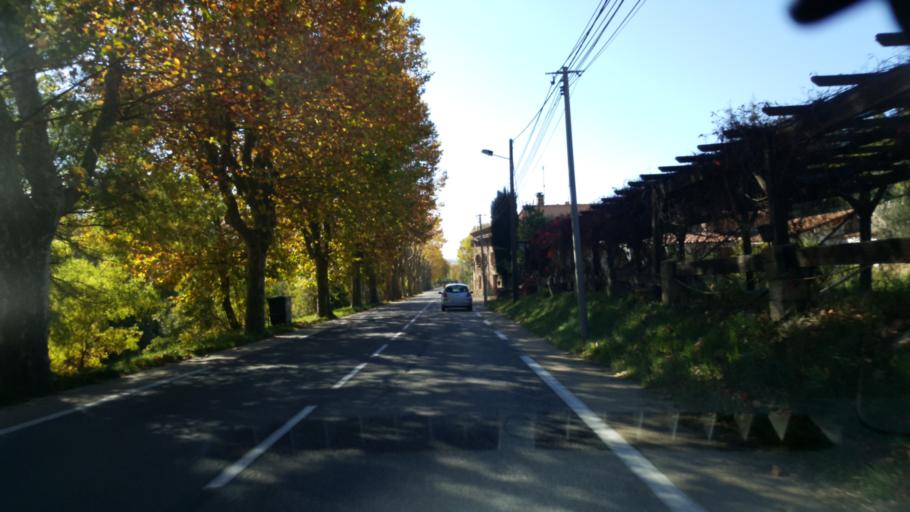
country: FR
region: Provence-Alpes-Cote d'Azur
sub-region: Departement du Var
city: Saint-Zacharie
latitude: 43.3874
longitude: 5.7177
